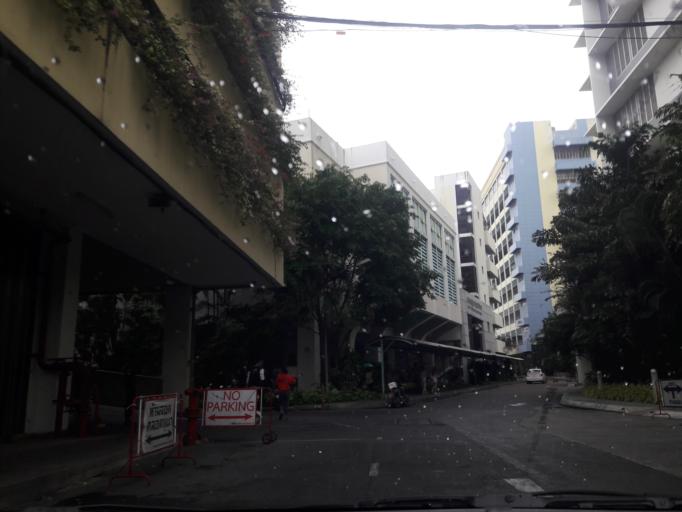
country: TH
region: Bangkok
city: Bang Kapi
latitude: 13.7701
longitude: 100.6542
